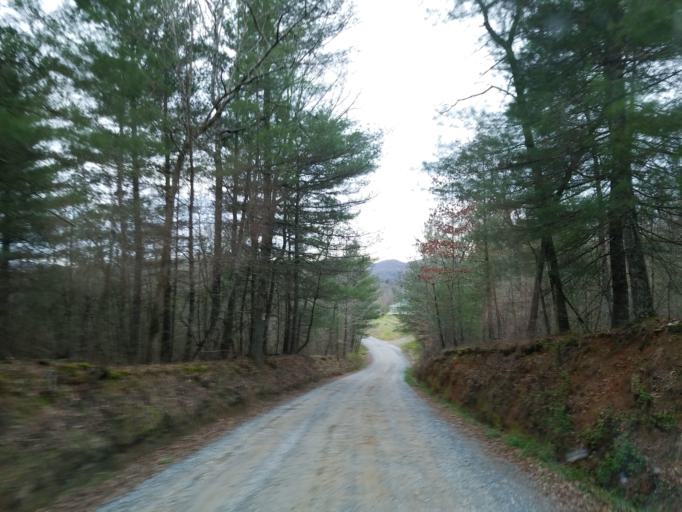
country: US
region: Georgia
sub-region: Gilmer County
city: Ellijay
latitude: 34.6525
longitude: -84.3066
